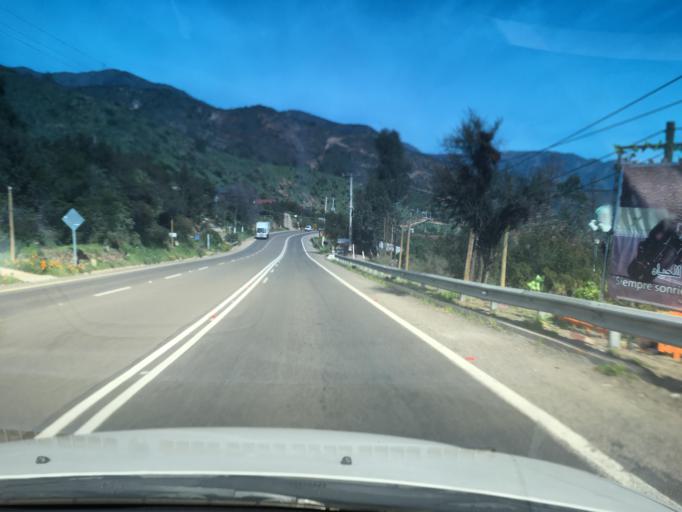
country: CL
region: Valparaiso
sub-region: Provincia de Marga Marga
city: Limache
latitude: -33.0580
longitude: -71.0460
